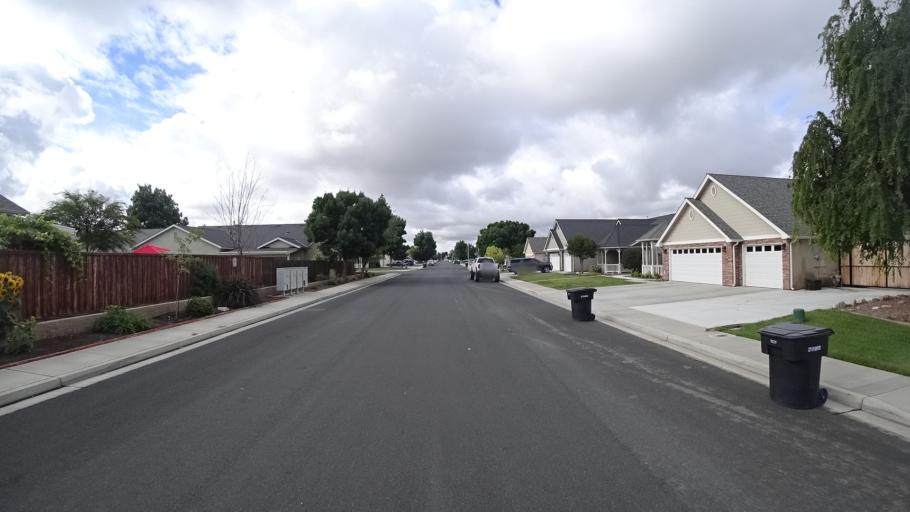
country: US
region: California
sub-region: Kings County
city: Lucerne
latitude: 36.3547
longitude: -119.6722
